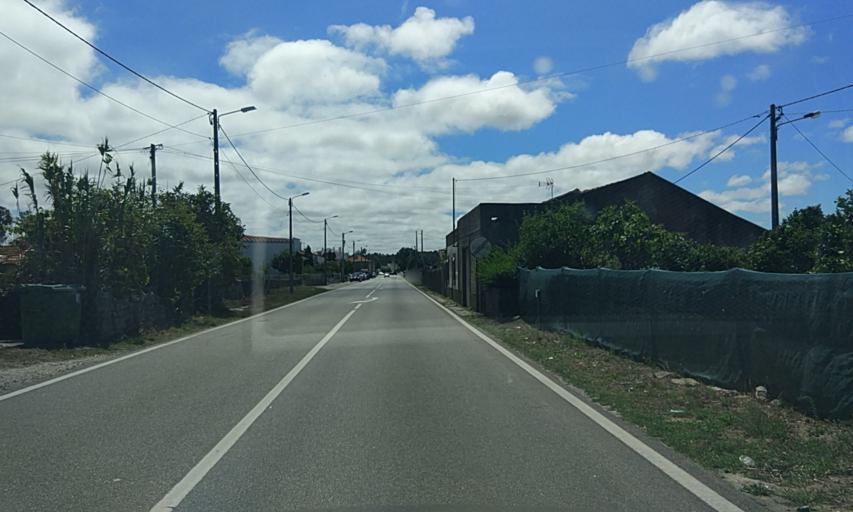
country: PT
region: Aveiro
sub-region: Vagos
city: Vagos
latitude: 40.5258
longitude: -8.6794
